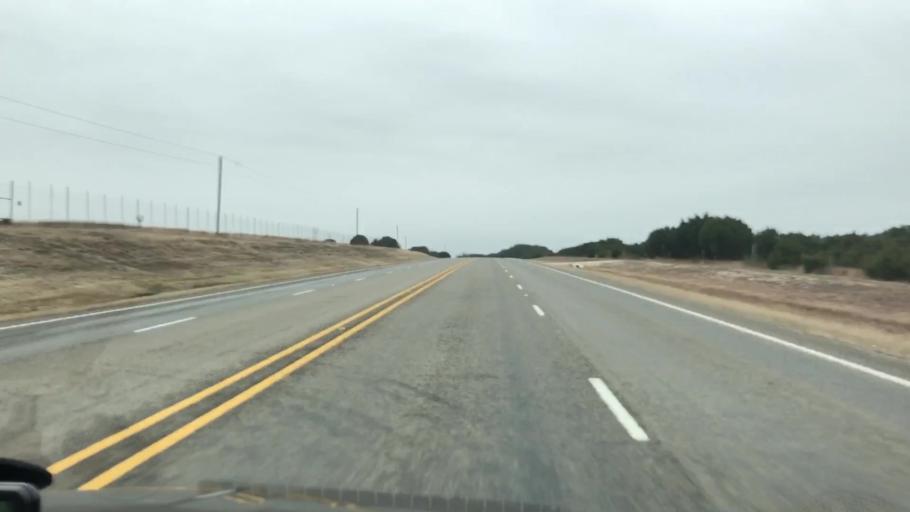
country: US
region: Texas
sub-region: Lampasas County
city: Lampasas
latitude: 31.1842
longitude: -98.1726
